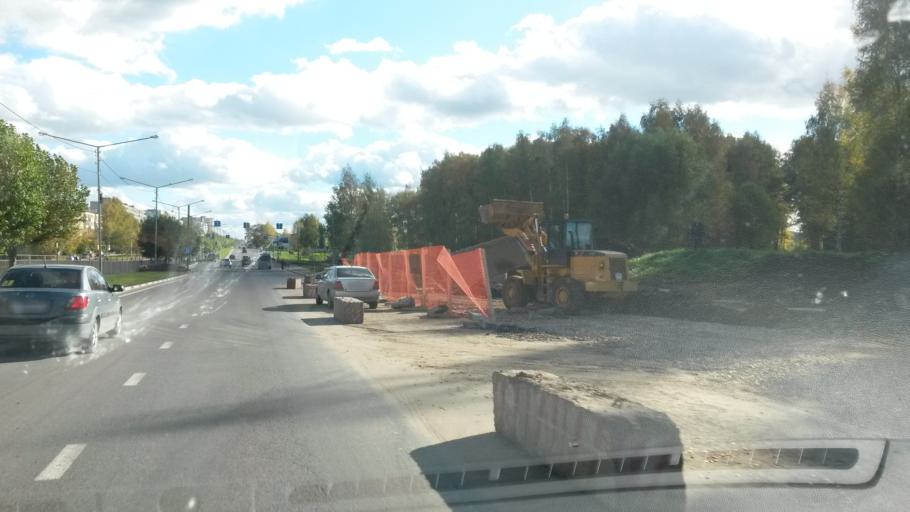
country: RU
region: Jaroslavl
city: Yaroslavl
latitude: 57.5762
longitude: 39.9168
